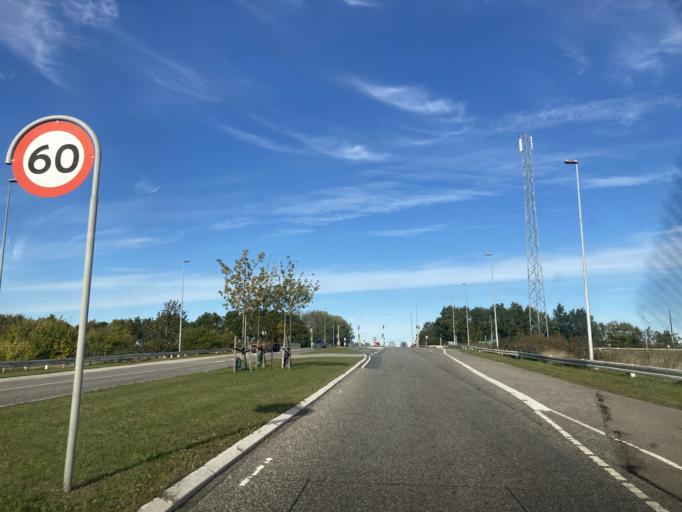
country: DK
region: Capital Region
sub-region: Vallensbaek Kommune
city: Vallensbaek
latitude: 55.6408
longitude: 12.3728
